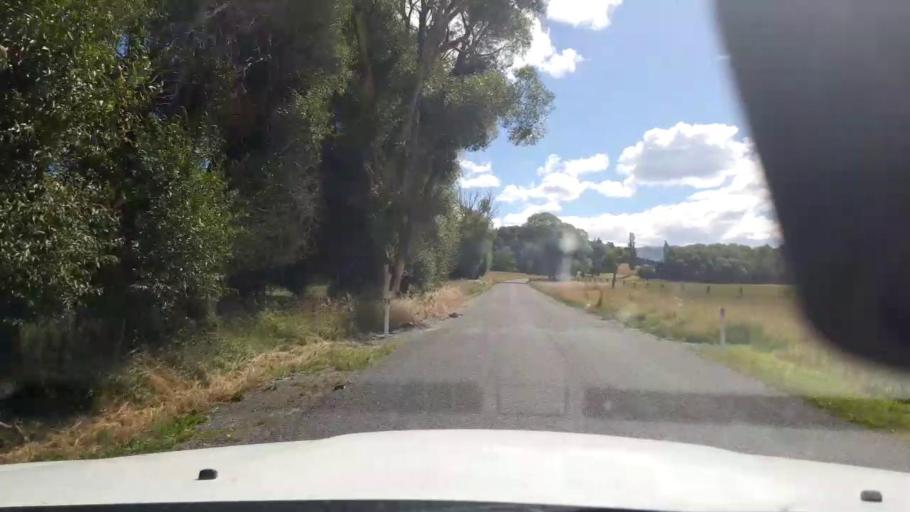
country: NZ
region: Canterbury
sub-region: Timaru District
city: Pleasant Point
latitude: -44.3177
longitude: 170.9439
